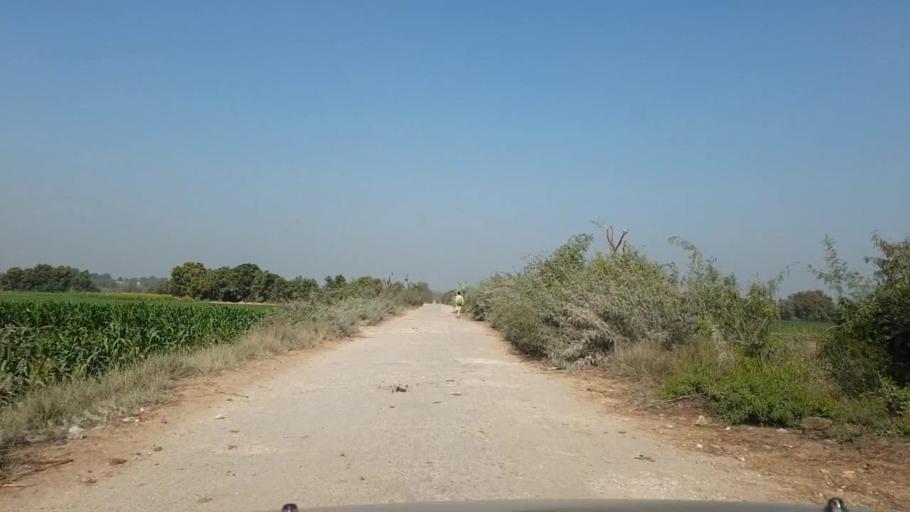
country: PK
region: Sindh
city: Matiari
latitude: 25.5792
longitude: 68.6040
